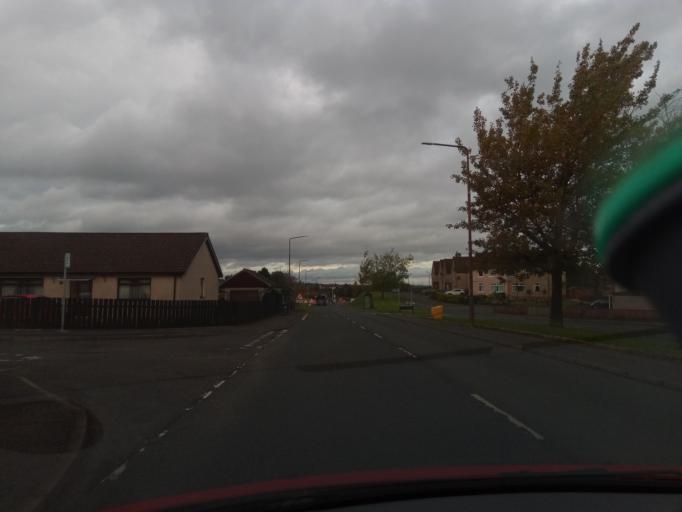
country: GB
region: Scotland
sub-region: West Lothian
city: Blackburn
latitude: 55.8428
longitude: -3.6165
